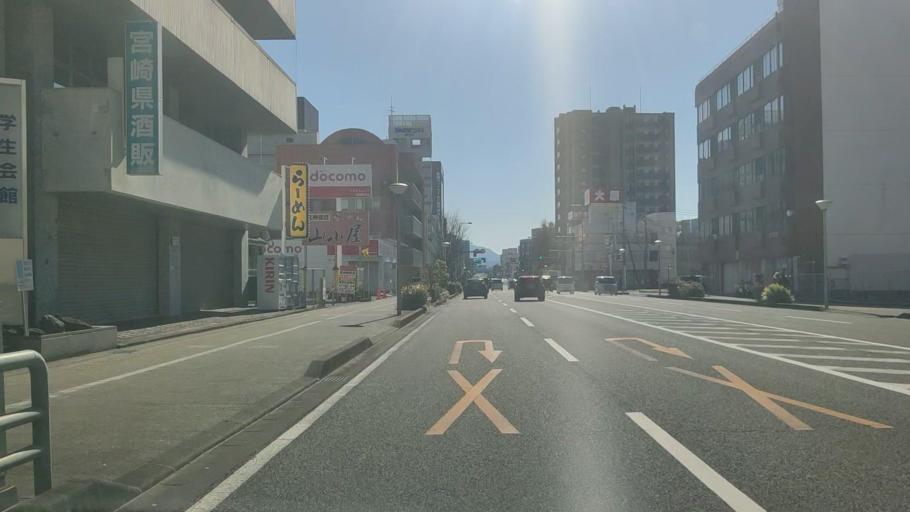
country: JP
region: Miyazaki
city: Miyazaki-shi
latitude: 31.9140
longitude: 131.4302
